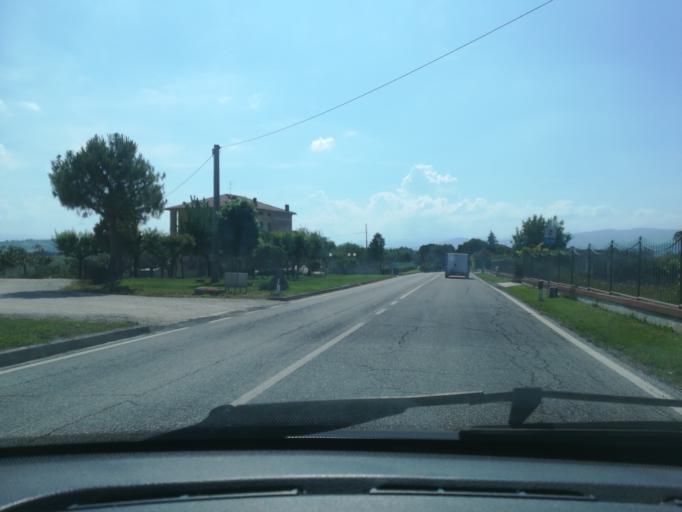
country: IT
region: The Marches
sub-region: Provincia di Macerata
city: Casette Verdini
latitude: 43.2873
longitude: 13.4013
